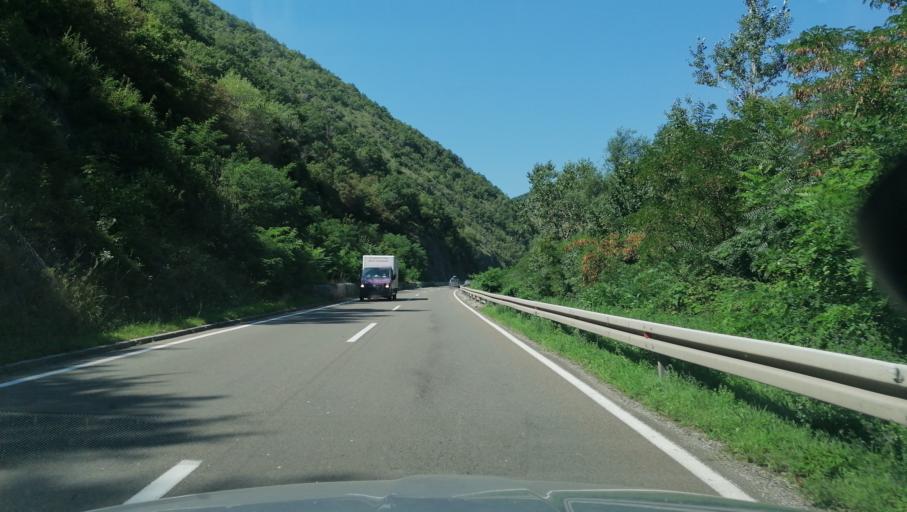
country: RS
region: Central Serbia
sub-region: Raski Okrug
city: Kraljevo
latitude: 43.6058
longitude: 20.5554
